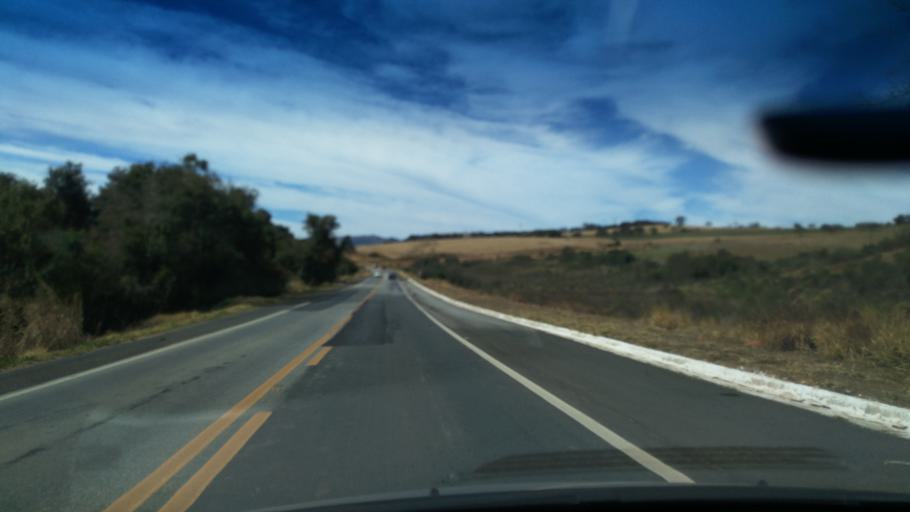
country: BR
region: Minas Gerais
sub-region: Borda Da Mata
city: Borda da Mata
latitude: -22.0616
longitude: -46.2797
